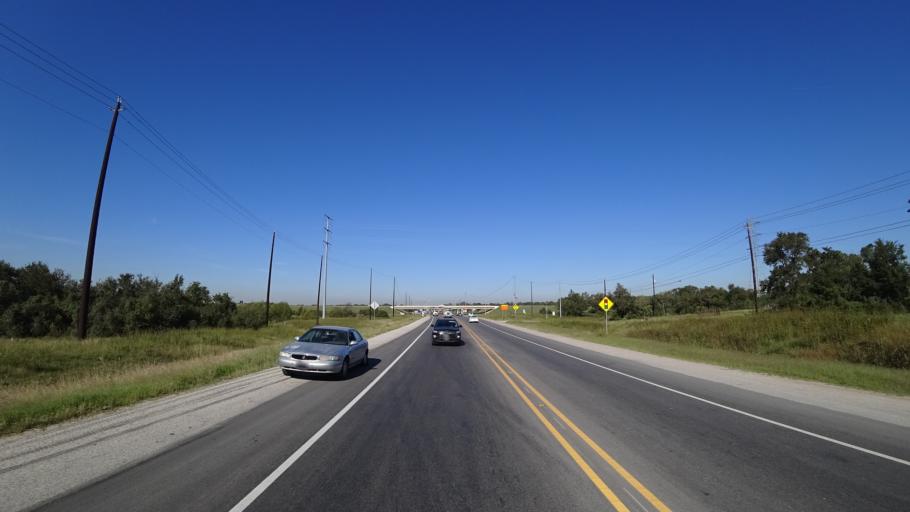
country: US
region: Texas
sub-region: Travis County
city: Hornsby Bend
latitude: 30.2523
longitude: -97.6008
